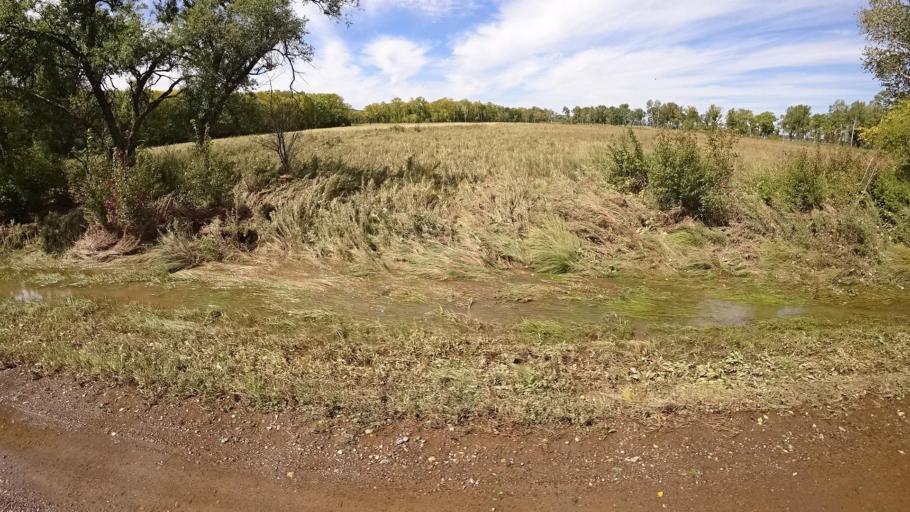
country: RU
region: Primorskiy
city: Yakovlevka
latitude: 44.6619
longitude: 133.7499
